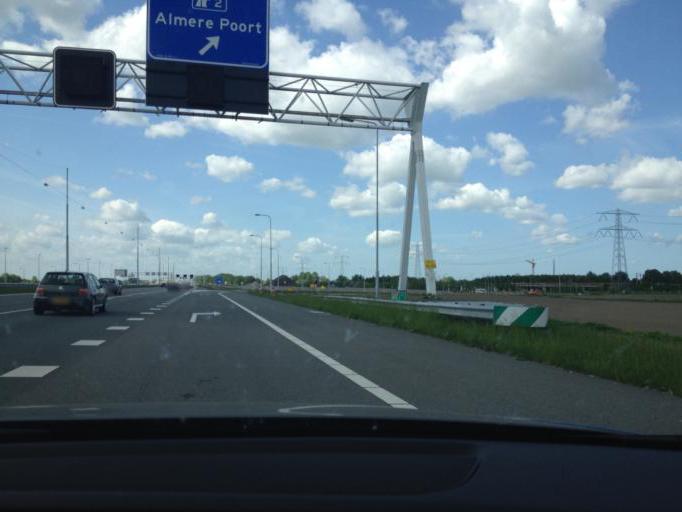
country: NL
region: North Holland
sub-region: Gemeente Naarden
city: Naarden
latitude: 52.3358
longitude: 5.1588
